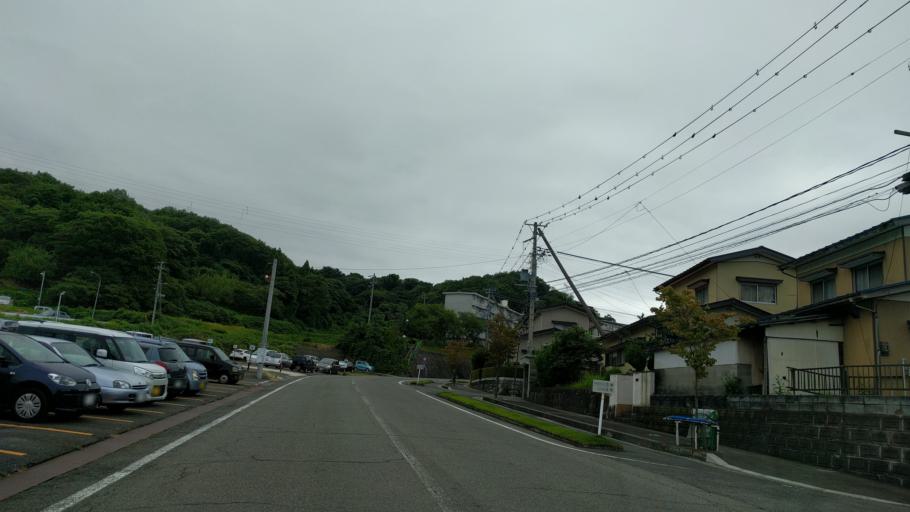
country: JP
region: Fukushima
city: Kitakata
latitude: 37.5197
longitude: 139.9504
